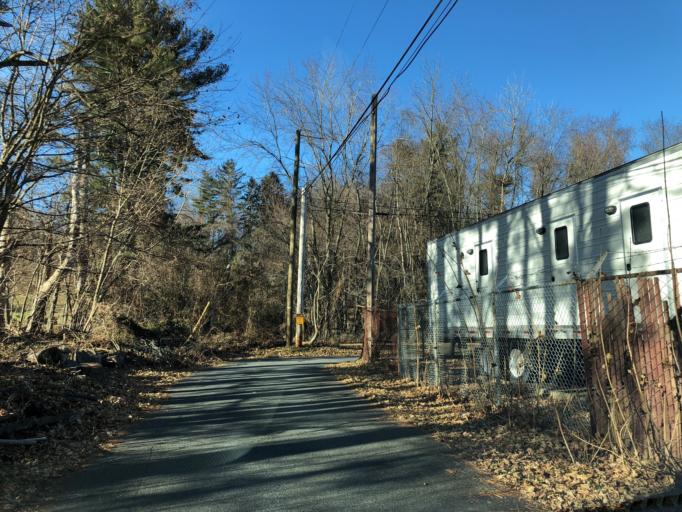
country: US
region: Maryland
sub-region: Baltimore County
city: Perry Hall
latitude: 39.4568
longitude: -76.4980
